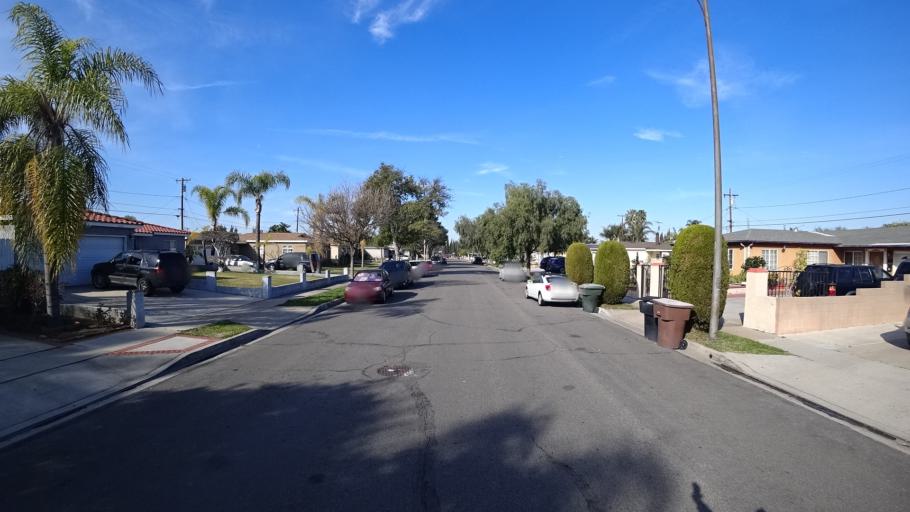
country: US
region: California
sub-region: Orange County
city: Fullerton
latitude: 33.8529
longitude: -117.9363
